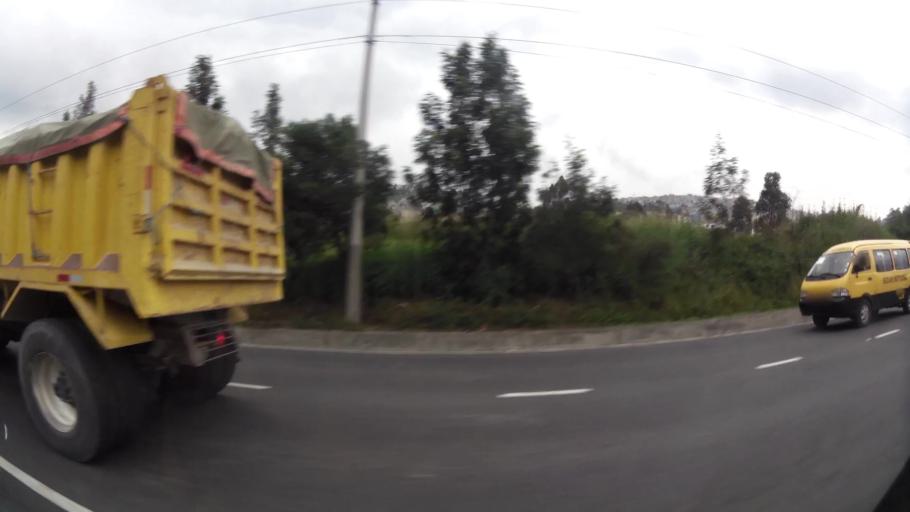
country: EC
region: Pichincha
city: Quito
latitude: -0.1162
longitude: -78.4538
